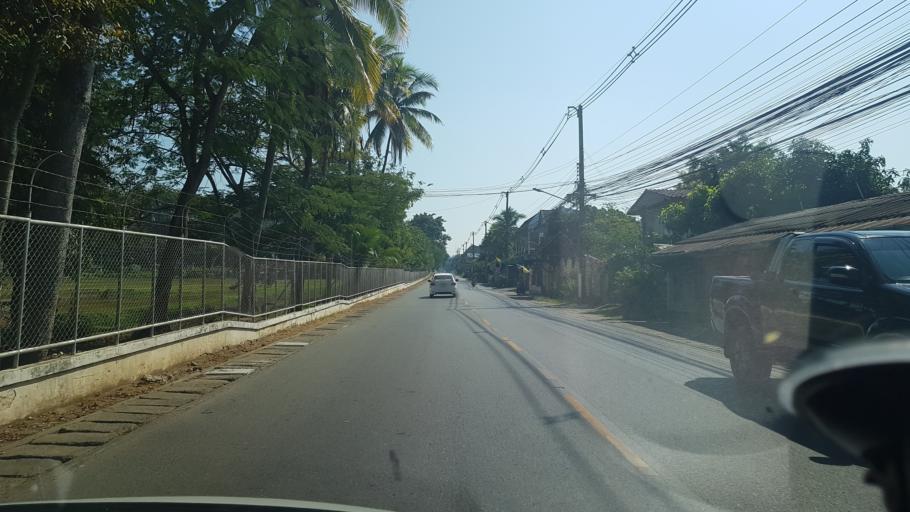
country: TH
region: Chiang Rai
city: Chiang Rai
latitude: 19.9058
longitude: 99.8087
